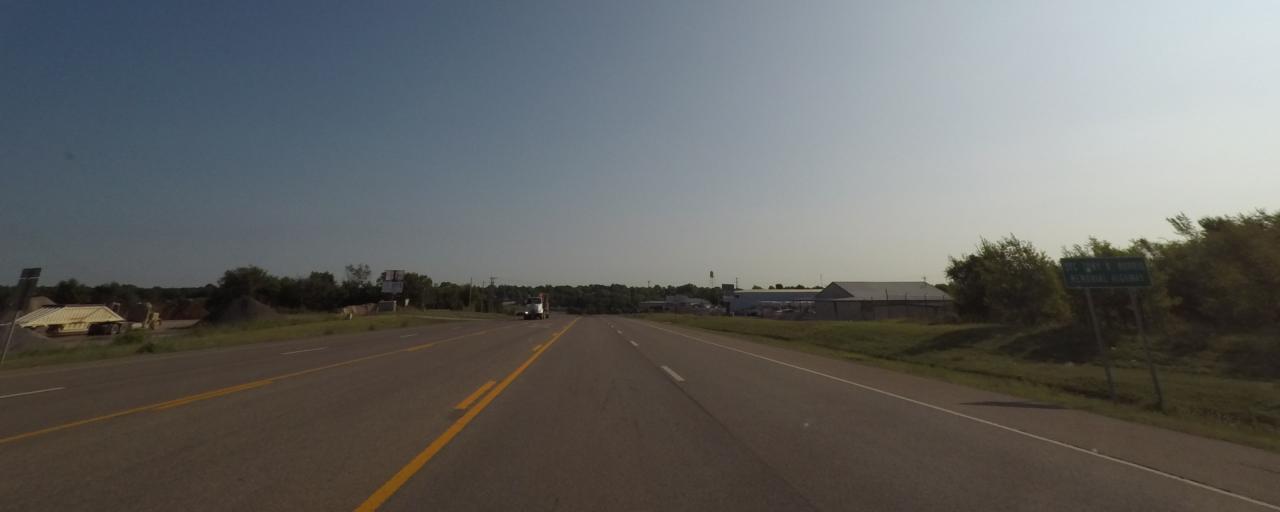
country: US
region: Oklahoma
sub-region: McClain County
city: Blanchard
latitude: 35.1293
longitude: -97.6683
